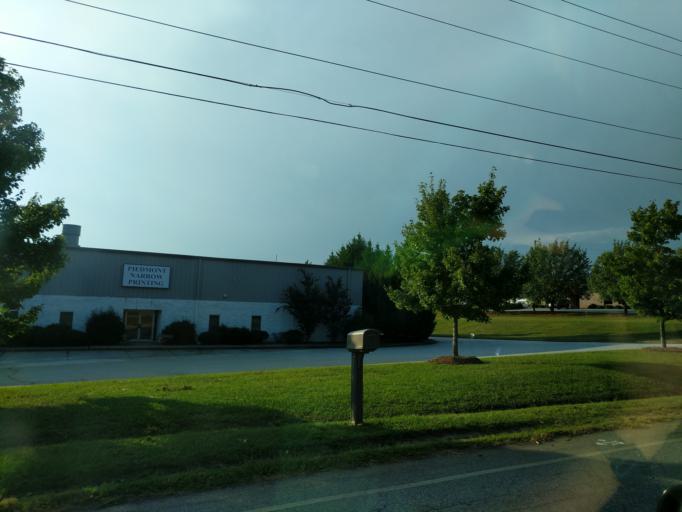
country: US
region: South Carolina
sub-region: Anderson County
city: Piedmont
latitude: 34.7000
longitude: -82.5045
